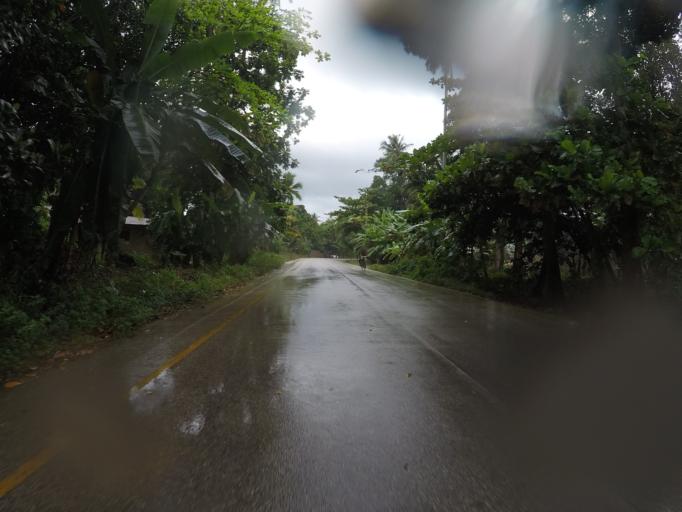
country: TZ
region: Zanzibar North
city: Mkokotoni
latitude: -5.9661
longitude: 39.1961
